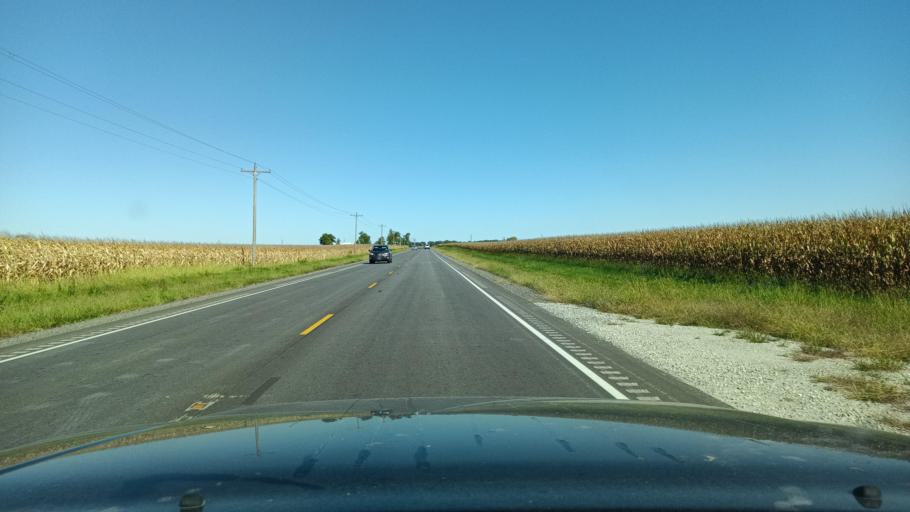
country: US
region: Illinois
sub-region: Champaign County
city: Philo
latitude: 39.9747
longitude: -88.1612
